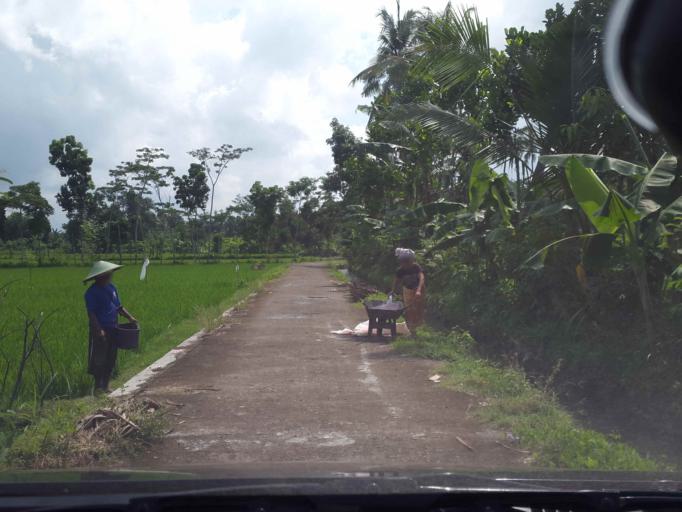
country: ID
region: West Nusa Tenggara
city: Jejelok
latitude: -8.6044
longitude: 116.1675
